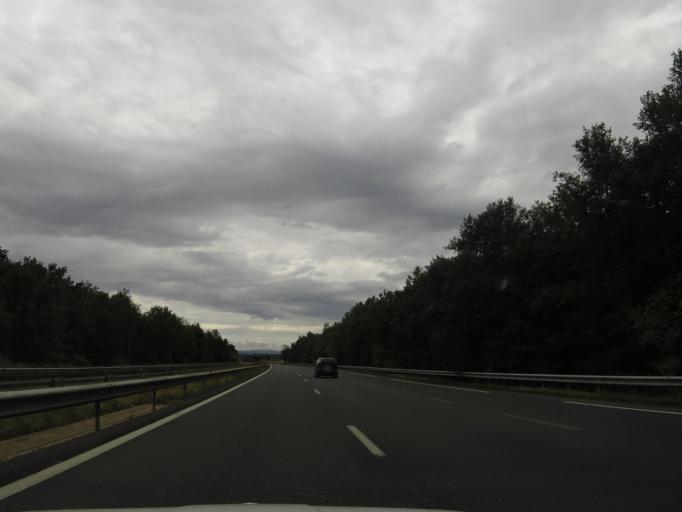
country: FR
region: Rhone-Alpes
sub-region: Departement de la Loire
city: Saint-Germain-Laval
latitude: 45.8424
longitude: 4.0896
